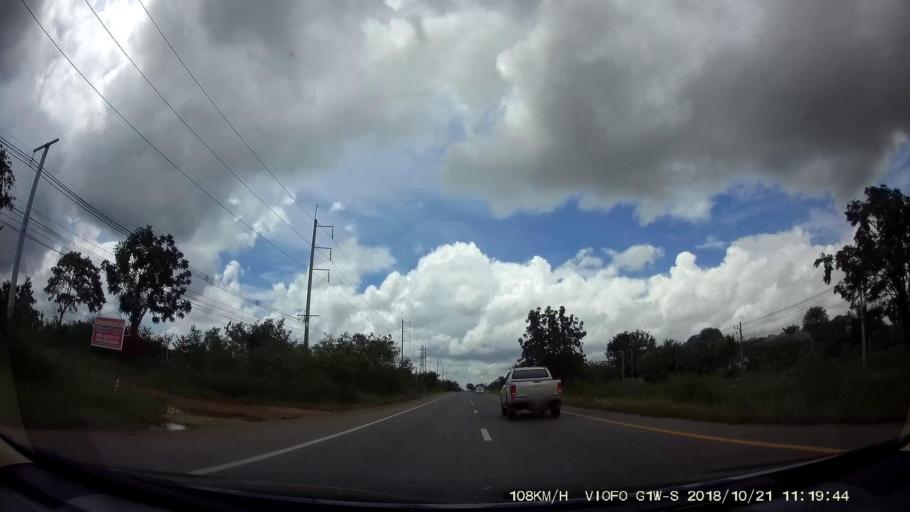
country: TH
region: Chaiyaphum
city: Chaiyaphum
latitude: 15.8647
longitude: 102.0828
